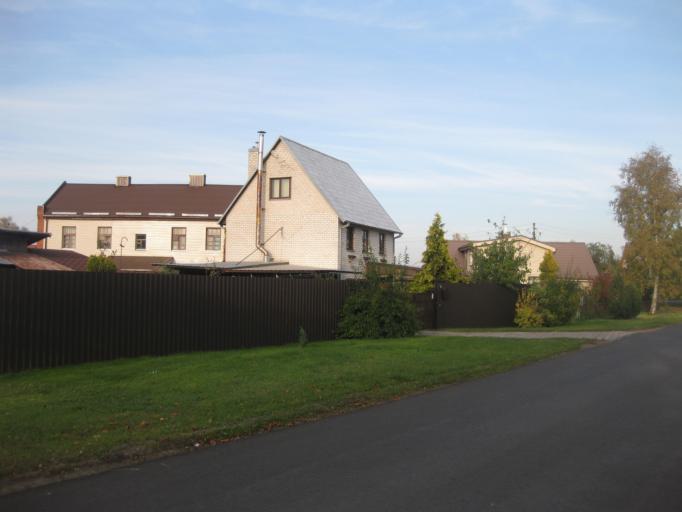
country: LT
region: Kauno apskritis
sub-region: Kaunas
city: Aleksotas
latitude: 54.8904
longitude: 23.8755
